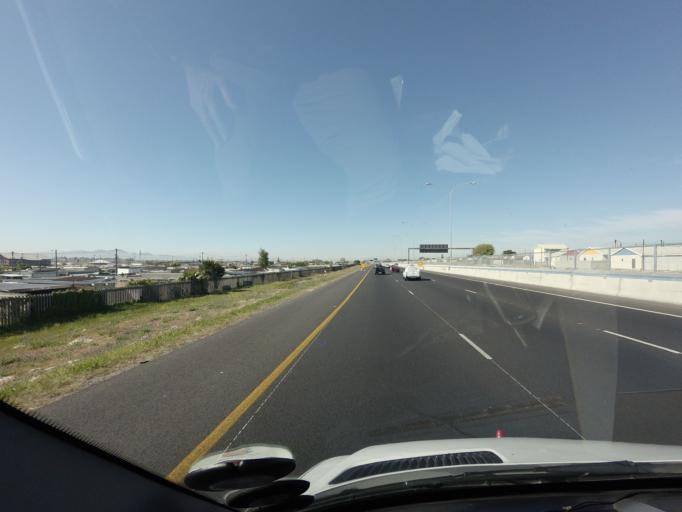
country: ZA
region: Western Cape
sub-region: City of Cape Town
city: Kraaifontein
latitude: -33.9635
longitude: 18.6557
